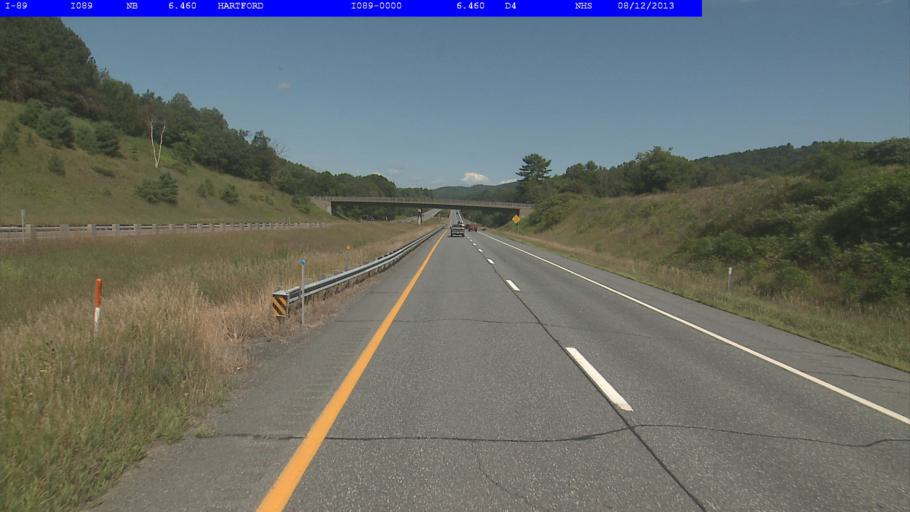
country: US
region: Vermont
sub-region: Windsor County
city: White River Junction
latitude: 43.6985
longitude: -72.4090
